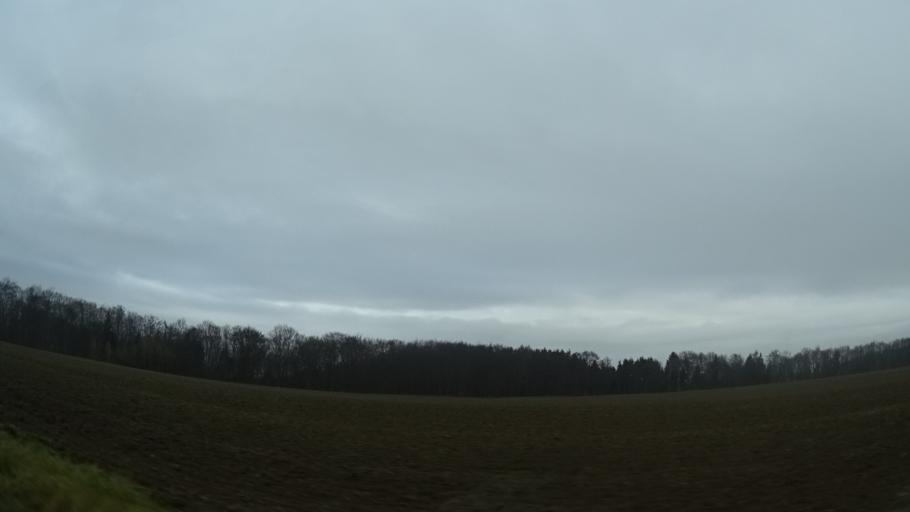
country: DE
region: Thuringia
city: Grossbockedra
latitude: 50.8376
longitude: 11.6602
